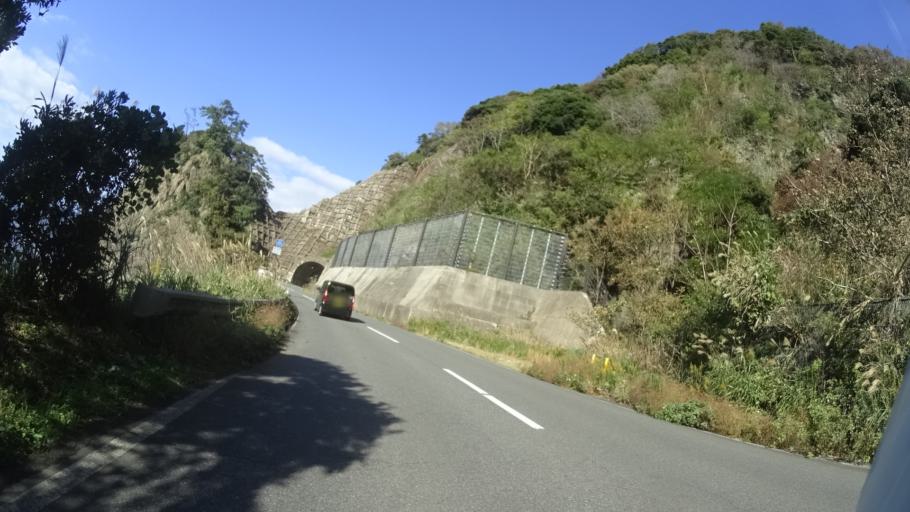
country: JP
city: Asahi
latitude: 35.9618
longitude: 135.9721
